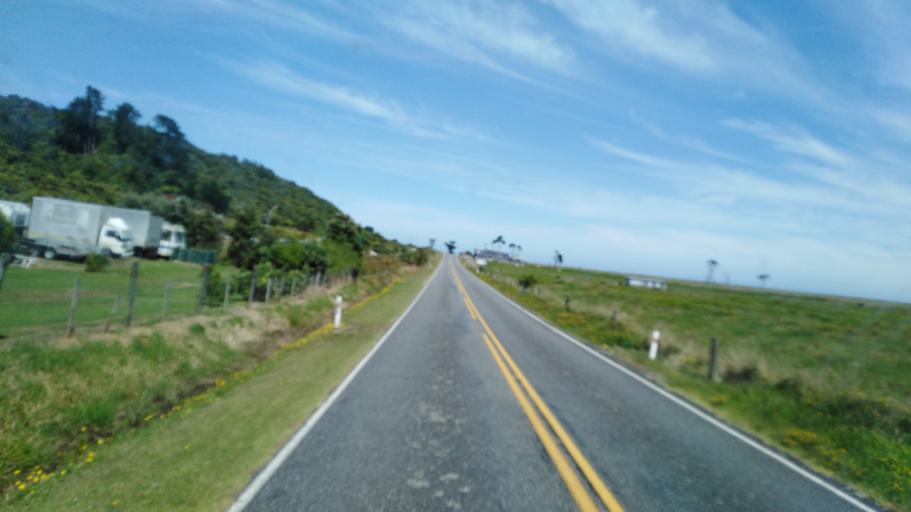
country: NZ
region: West Coast
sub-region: Buller District
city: Westport
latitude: -41.5320
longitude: 171.9393
